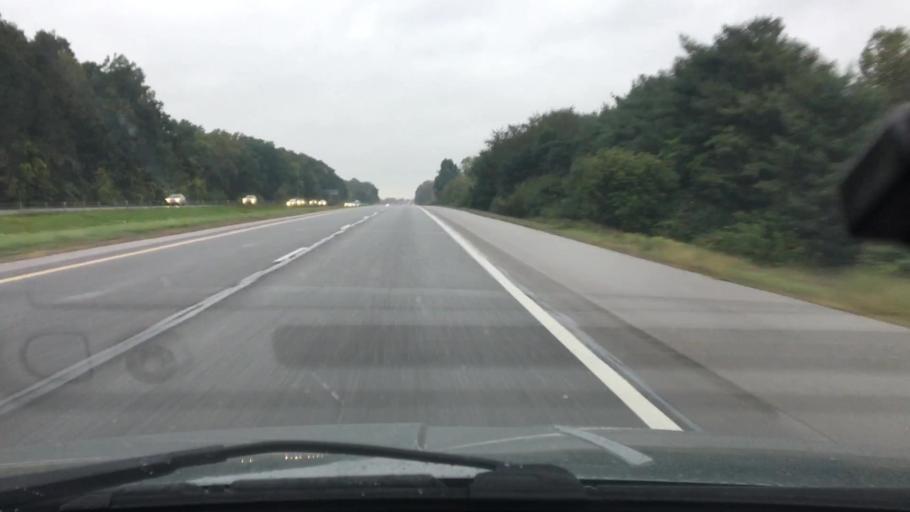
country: US
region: Michigan
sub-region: Washtenaw County
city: Dexter
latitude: 42.2975
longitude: -83.9076
